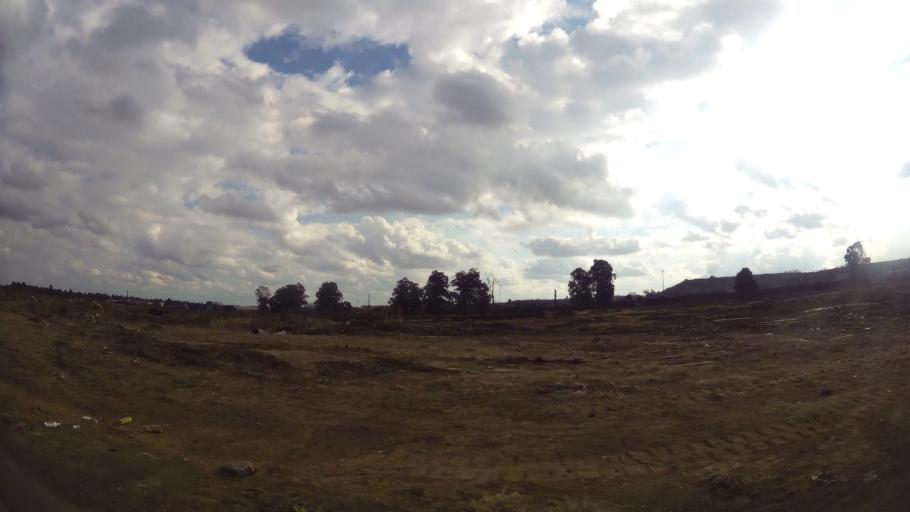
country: ZA
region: Orange Free State
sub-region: Fezile Dabi District Municipality
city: Sasolburg
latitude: -26.8407
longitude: 27.8400
